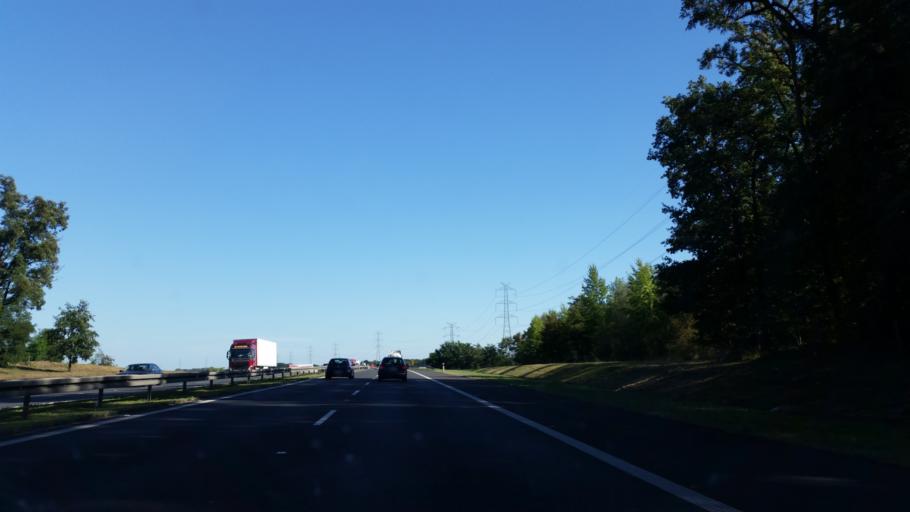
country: PL
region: Opole Voivodeship
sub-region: Powiat brzeski
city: Skarbimierz Osiedle
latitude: 50.7993
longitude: 17.3237
